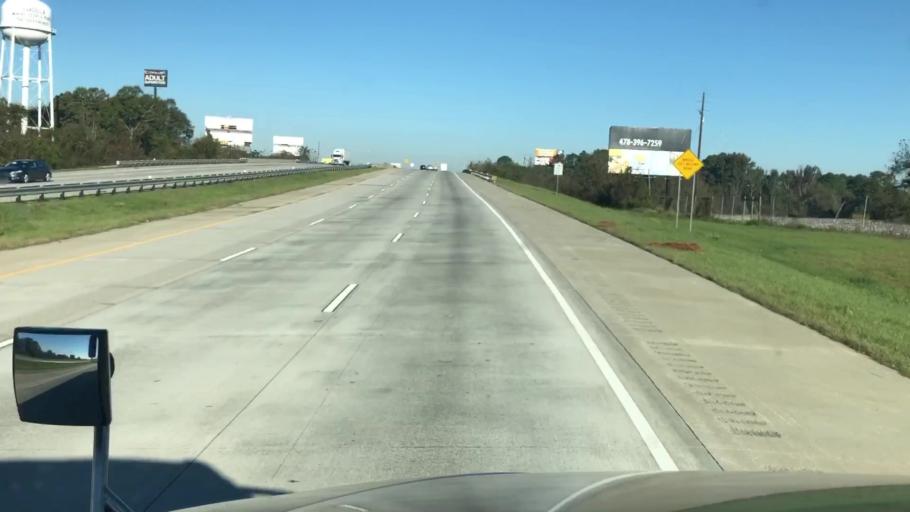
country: US
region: Georgia
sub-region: Dooly County
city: Unadilla
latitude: 32.2434
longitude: -83.7408
